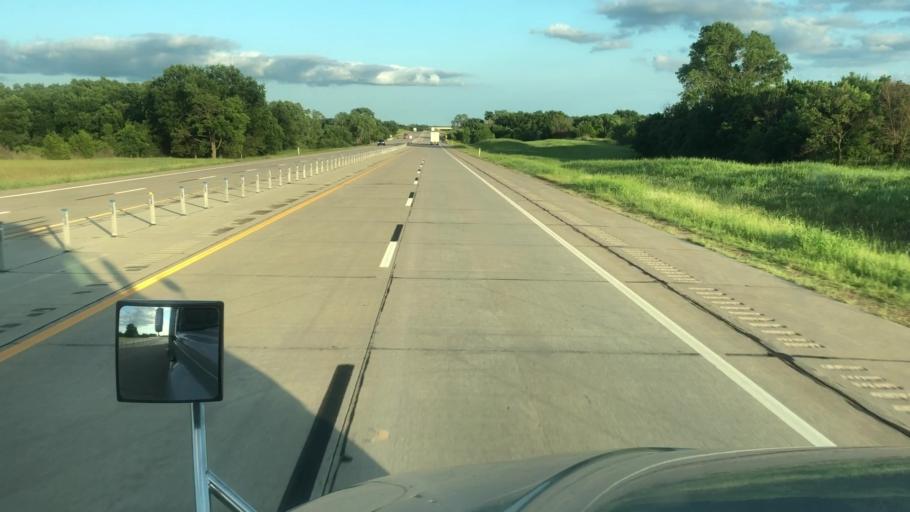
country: US
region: Oklahoma
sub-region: Pawnee County
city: Pawnee
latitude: 36.3271
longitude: -97.0068
